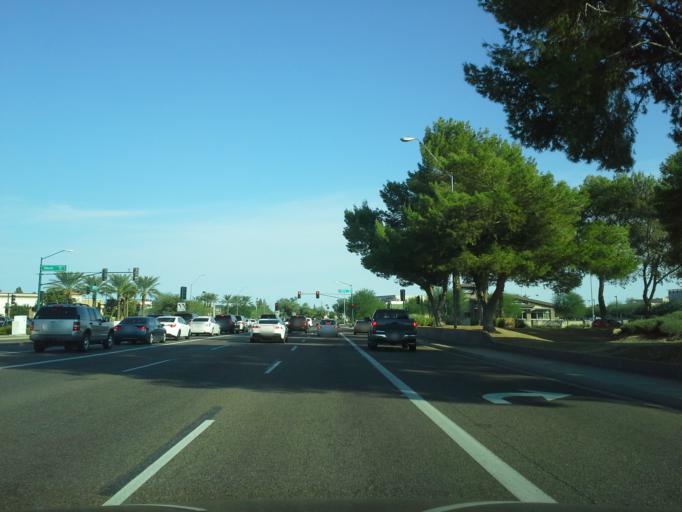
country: US
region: Arizona
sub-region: Maricopa County
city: Paradise Valley
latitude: 33.5989
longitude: -111.9814
